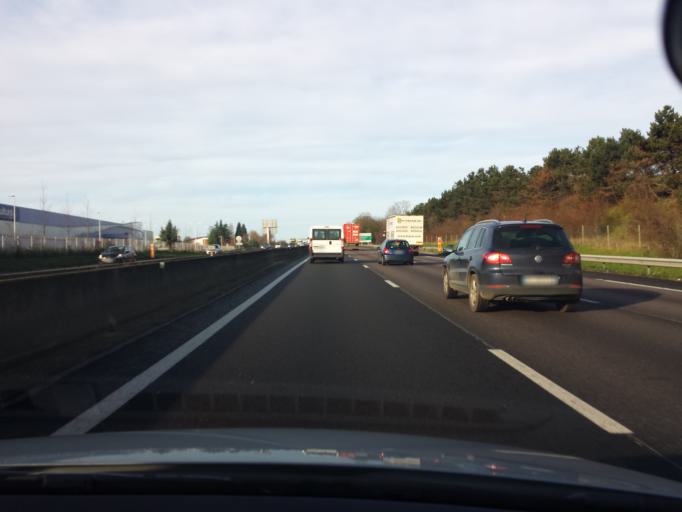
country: FR
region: Ile-de-France
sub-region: Departement des Yvelines
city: Orgeval
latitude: 48.9296
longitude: 1.9852
